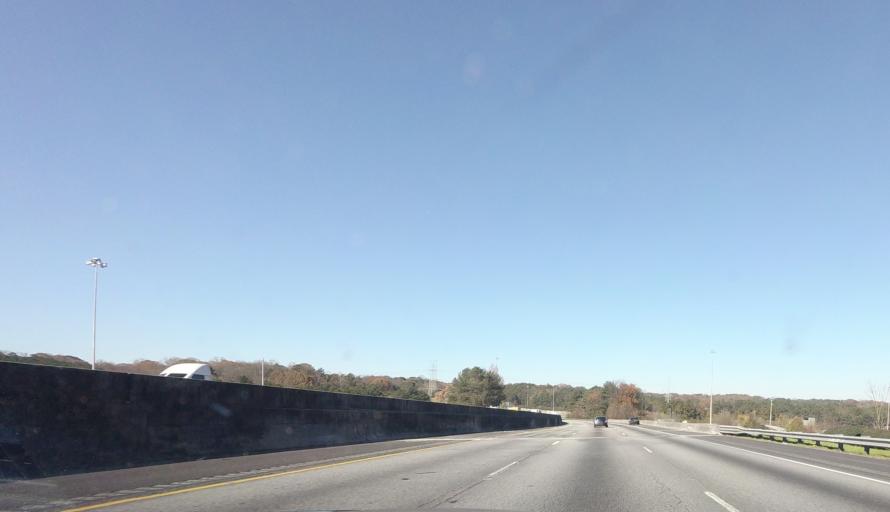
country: US
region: Georgia
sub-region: Fulton County
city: East Point
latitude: 33.7645
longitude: -84.4924
